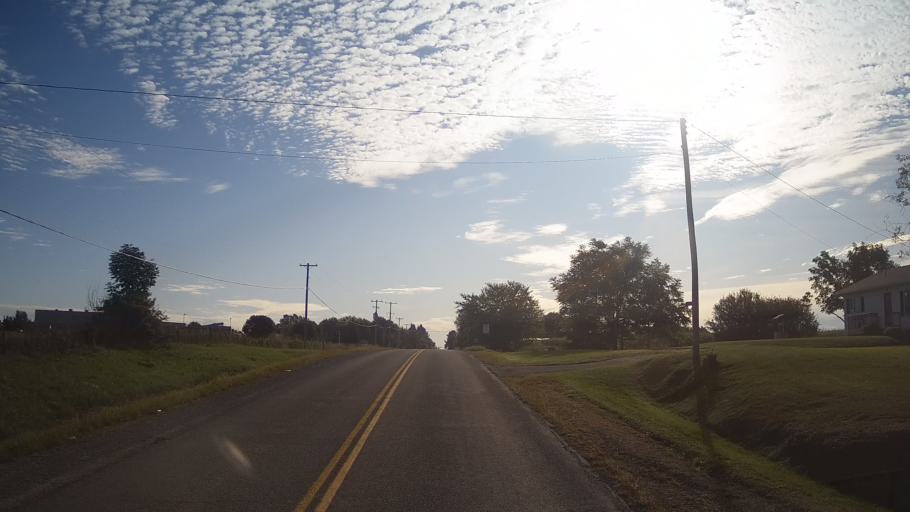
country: US
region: New York
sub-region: Jefferson County
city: Alexandria Bay
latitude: 44.4049
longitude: -76.0287
